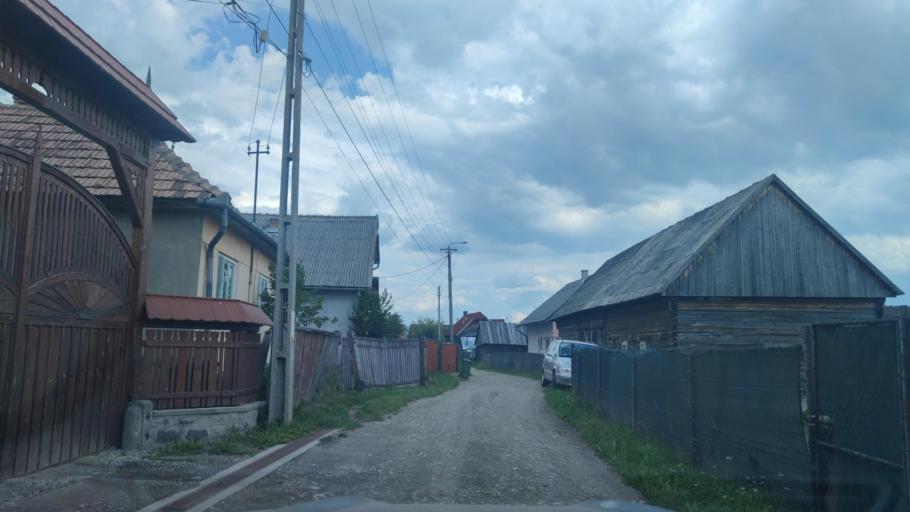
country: RO
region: Harghita
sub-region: Comuna Remetea
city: Remetea
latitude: 46.7960
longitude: 25.4344
